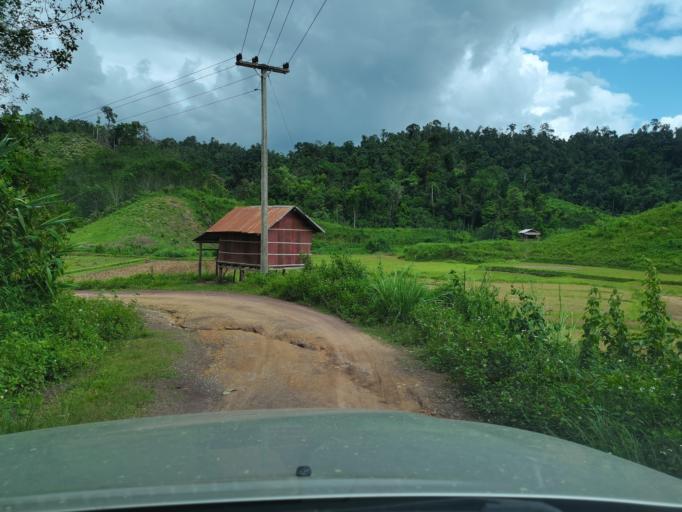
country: LA
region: Loungnamtha
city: Muang Long
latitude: 20.7007
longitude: 101.0170
